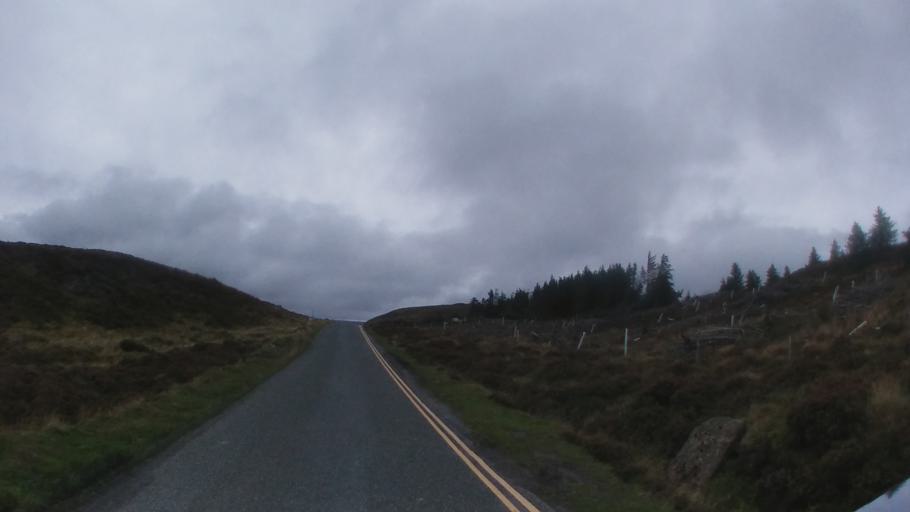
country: IE
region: Leinster
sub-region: Wicklow
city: Enniskerry
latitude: 53.1032
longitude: -6.2548
